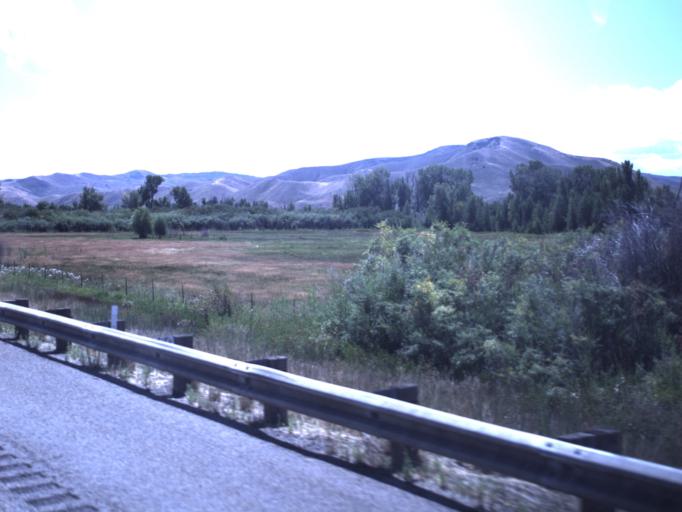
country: US
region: Utah
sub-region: Summit County
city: Coalville
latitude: 41.0355
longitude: -111.5097
